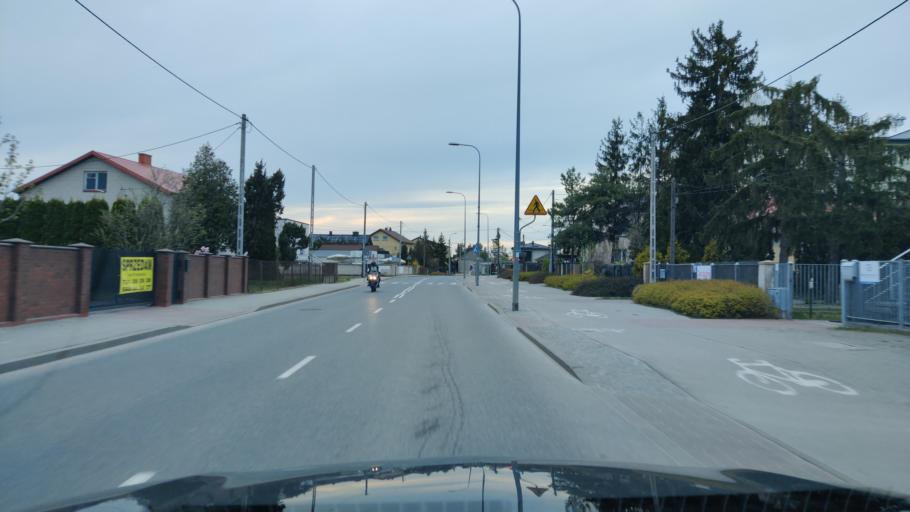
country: PL
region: Masovian Voivodeship
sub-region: Warszawa
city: Kabaty
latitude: 52.1311
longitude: 21.1021
